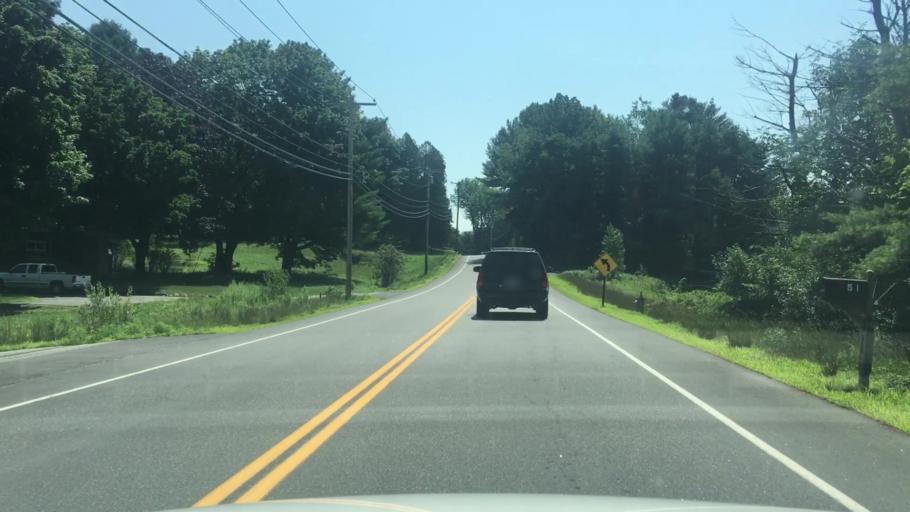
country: US
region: Maine
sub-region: Cumberland County
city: Cumberland Center
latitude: 43.8004
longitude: -70.2664
